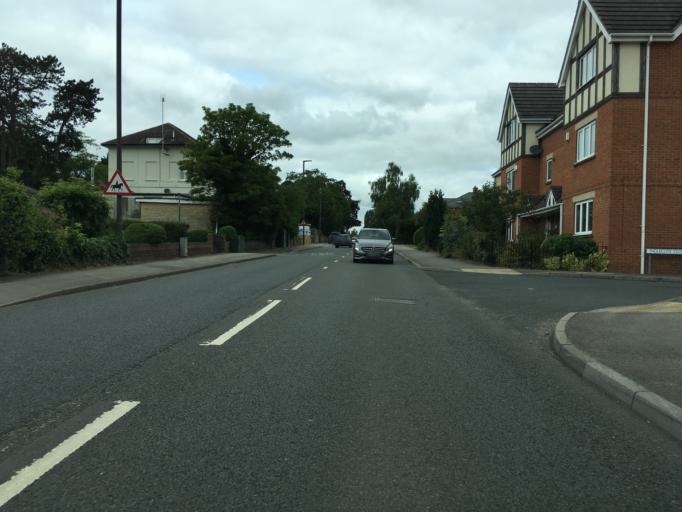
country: GB
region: England
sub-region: Gloucestershire
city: Charlton Kings
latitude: 51.8868
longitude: -2.0502
